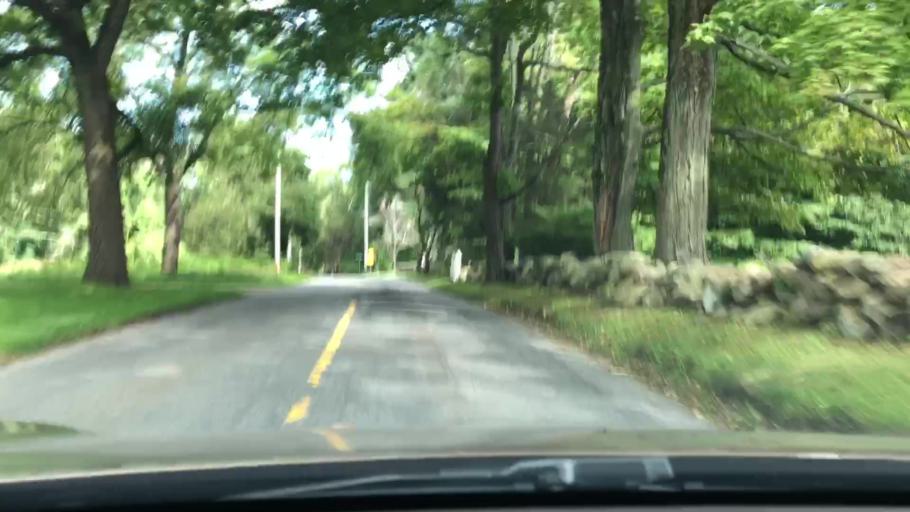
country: US
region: Connecticut
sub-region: Fairfield County
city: Darien
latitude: 41.1128
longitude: -73.4735
